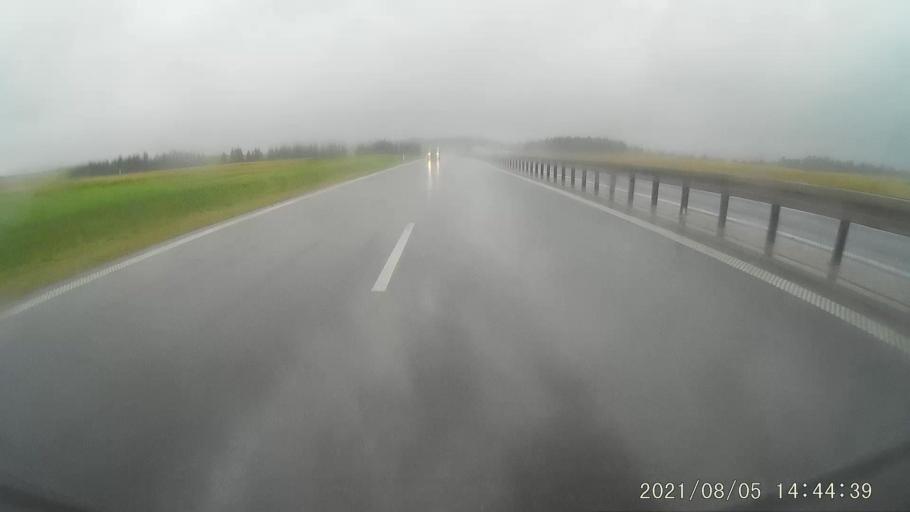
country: PL
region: Opole Voivodeship
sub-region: Powiat nyski
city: Nysa
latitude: 50.4954
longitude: 17.3741
